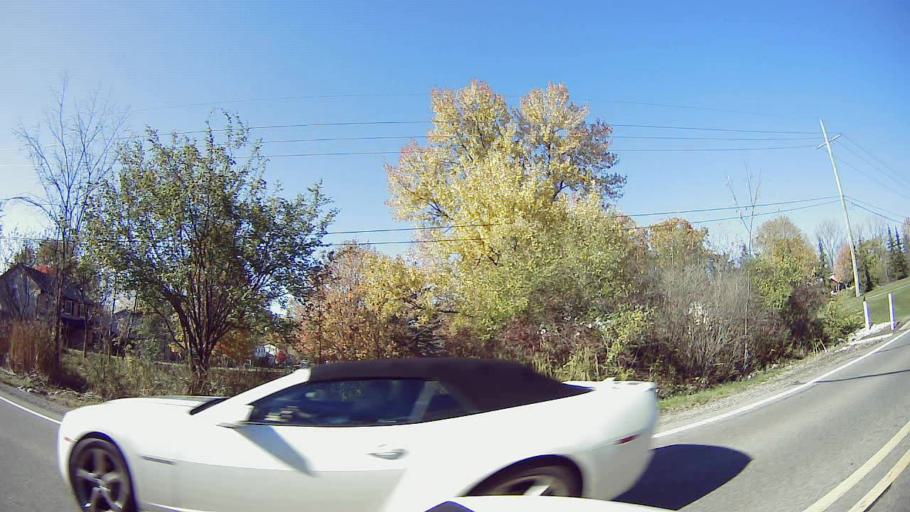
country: US
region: Michigan
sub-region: Oakland County
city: Farmington Hills
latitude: 42.5248
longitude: -83.3795
